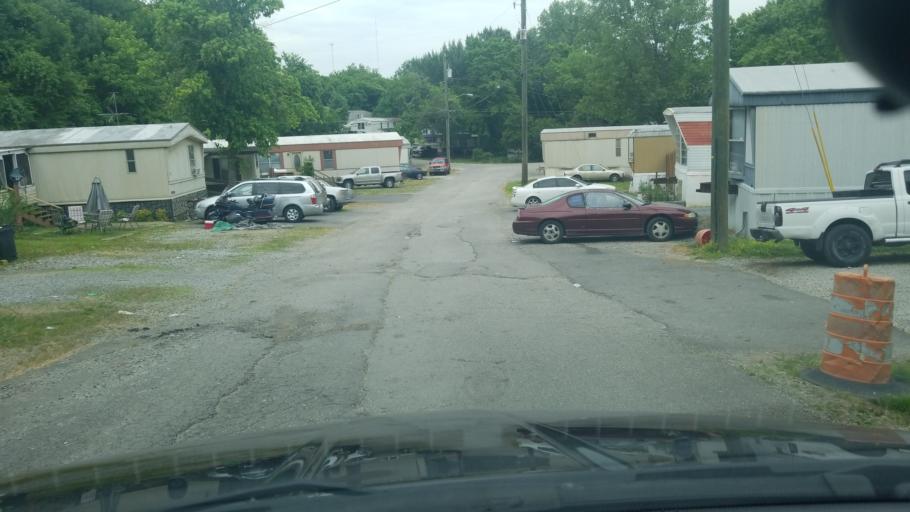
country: US
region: Tennessee
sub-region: Davidson County
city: Goodlettsville
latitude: 36.2588
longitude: -86.7538
